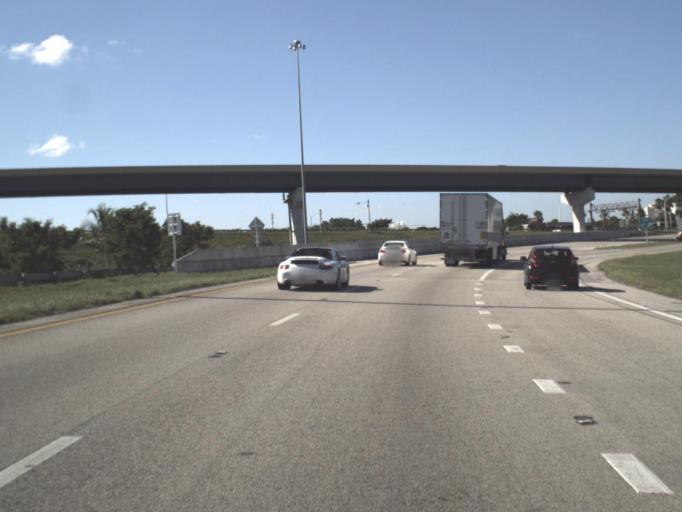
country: US
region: Florida
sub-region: Broward County
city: Miramar
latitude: 25.9743
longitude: -80.2308
